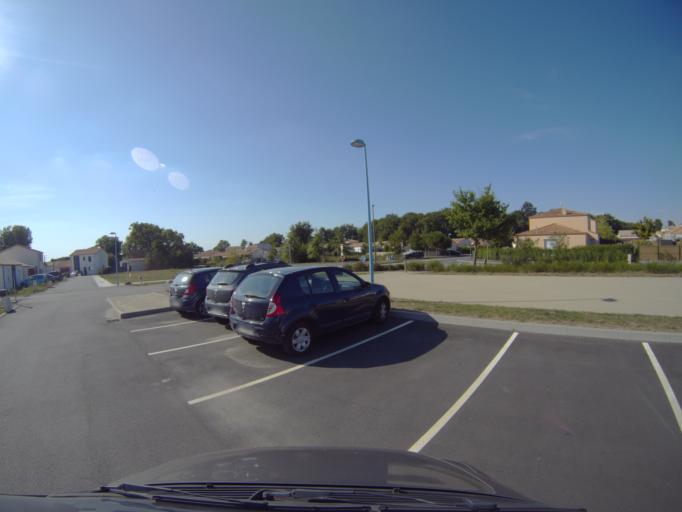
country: FR
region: Pays de la Loire
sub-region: Departement de la Loire-Atlantique
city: Gorges
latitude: 47.0881
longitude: -1.3026
